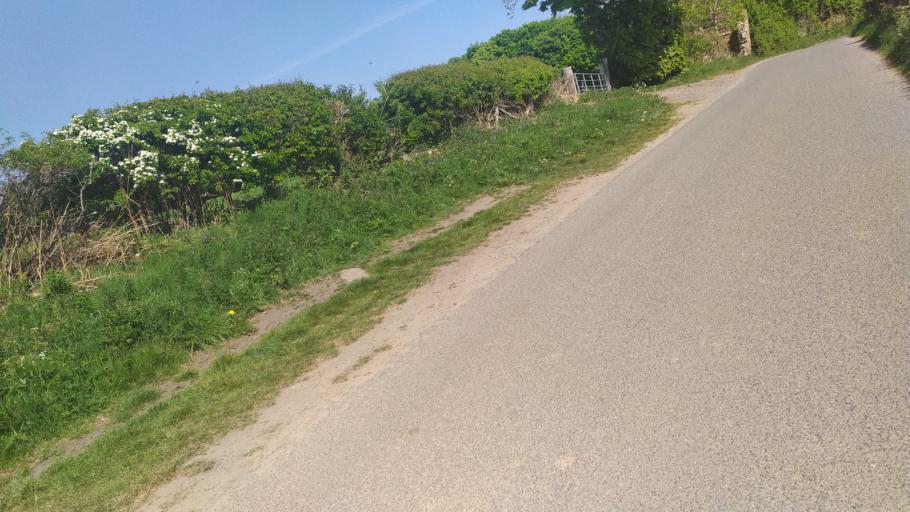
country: GB
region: England
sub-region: City and Borough of Leeds
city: Chapel Allerton
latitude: 53.8750
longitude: -1.5629
